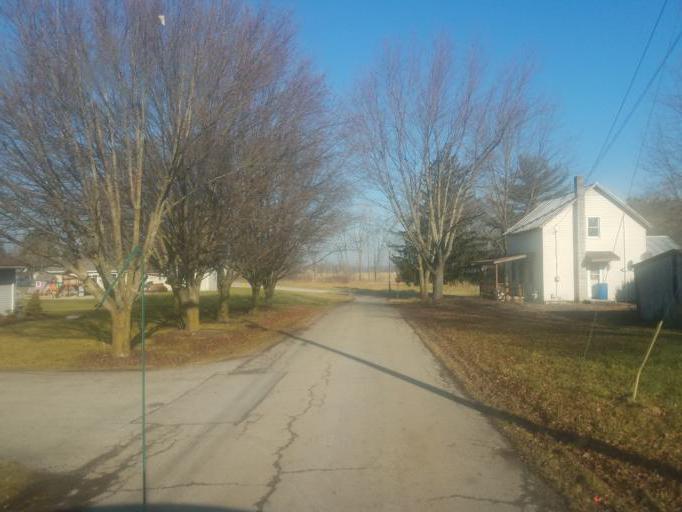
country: US
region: Ohio
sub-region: Seneca County
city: Tiffin
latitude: 41.0539
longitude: -83.0126
